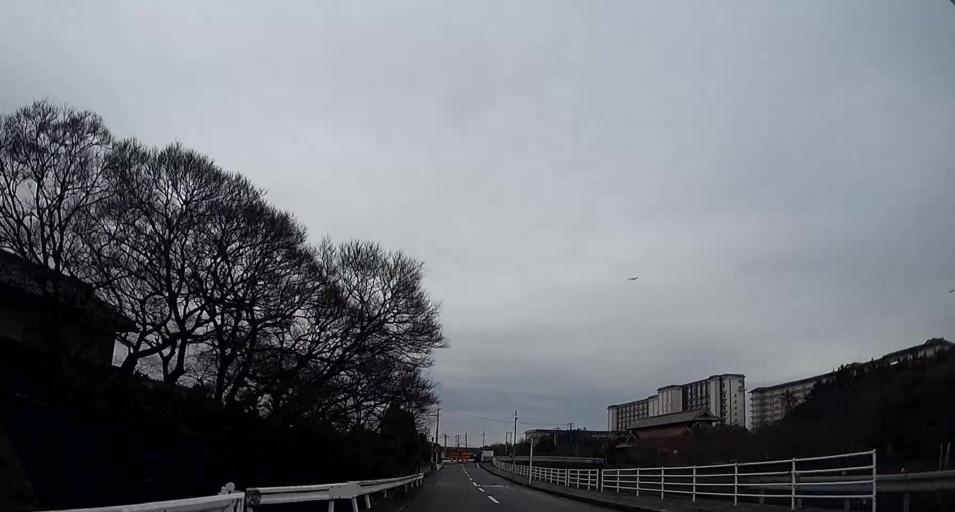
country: JP
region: Chiba
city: Kisarazu
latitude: 35.4226
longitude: 139.8999
